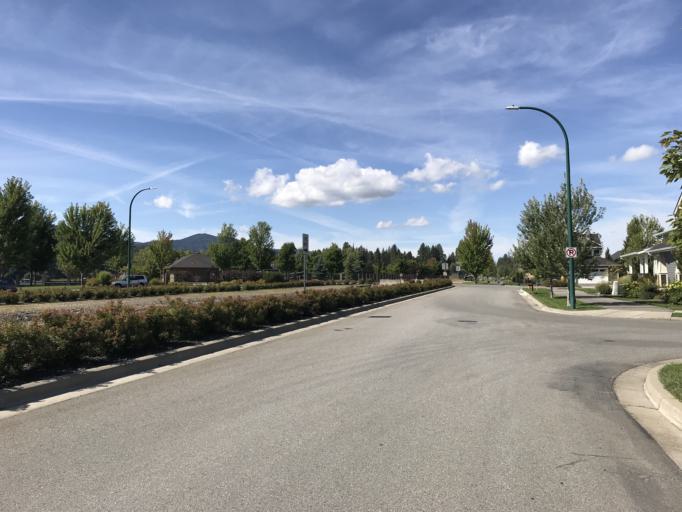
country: US
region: Idaho
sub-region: Kootenai County
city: Coeur d'Alene
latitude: 47.7011
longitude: -116.8437
